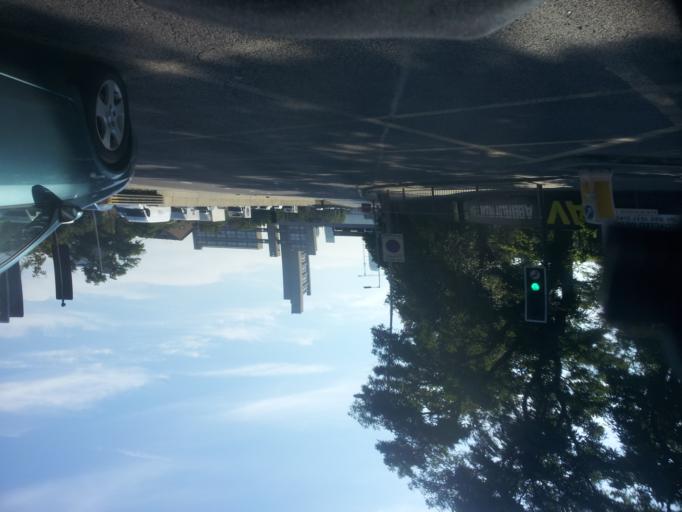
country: GB
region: England
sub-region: Greater London
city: Poplar
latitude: 51.5178
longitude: -0.0095
